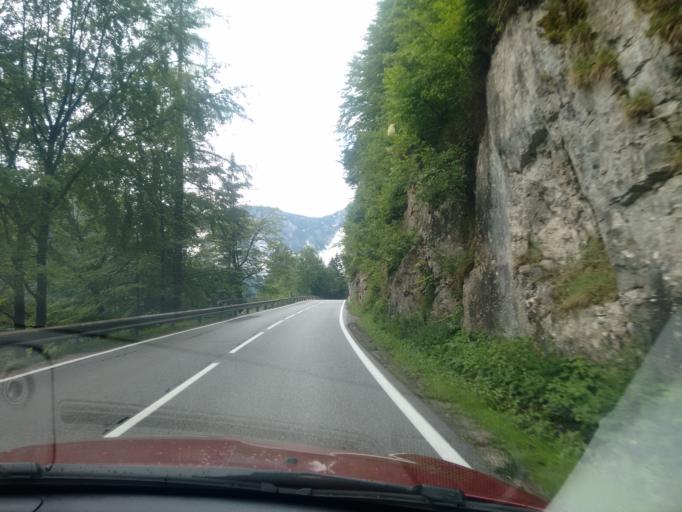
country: AT
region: Upper Austria
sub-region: Politischer Bezirk Gmunden
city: Bad Goisern
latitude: 47.5861
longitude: 13.6575
